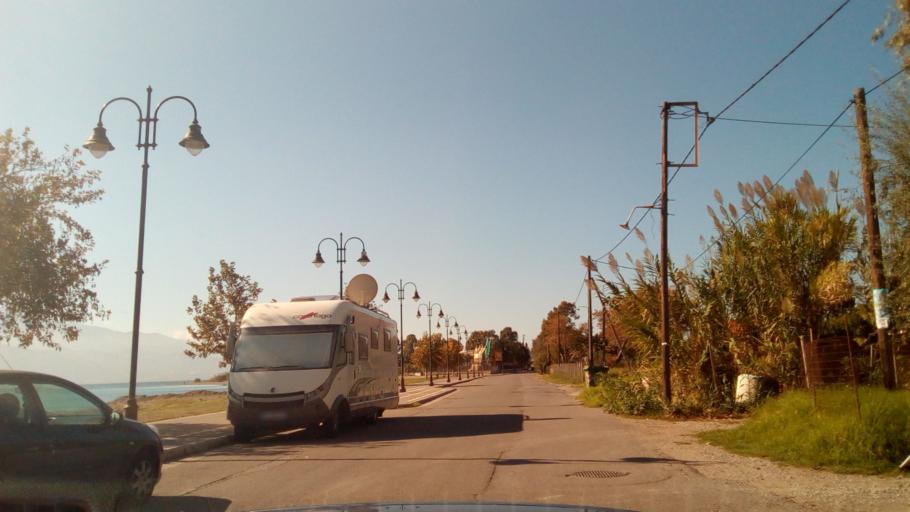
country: GR
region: West Greece
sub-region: Nomos Aitolias kai Akarnanias
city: Nafpaktos
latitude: 38.3855
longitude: 21.8198
